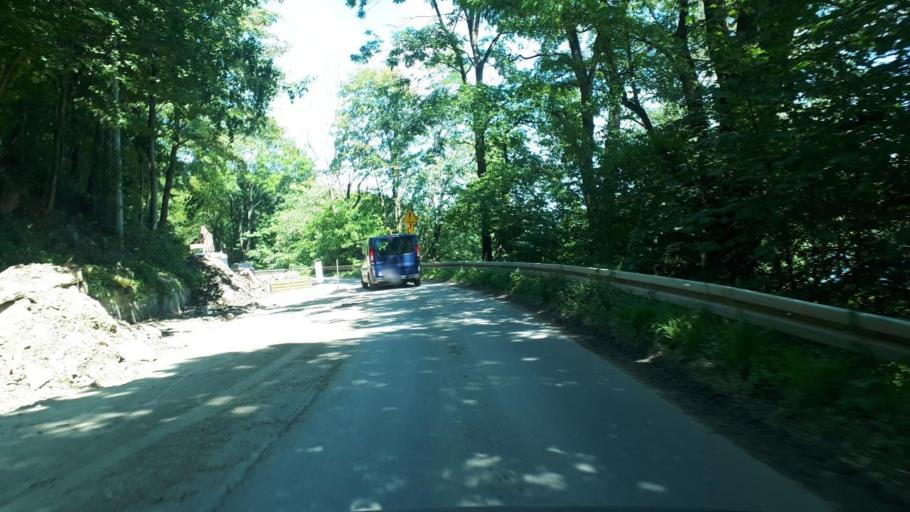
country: PL
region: Silesian Voivodeship
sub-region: Powiat zywiecki
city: Czernichow
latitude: 49.7630
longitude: 19.2072
